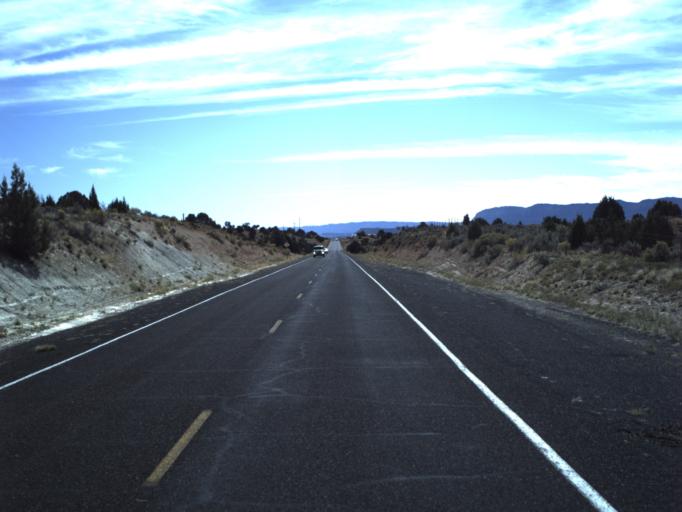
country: US
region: Utah
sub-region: Wayne County
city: Loa
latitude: 37.7549
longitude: -111.5698
